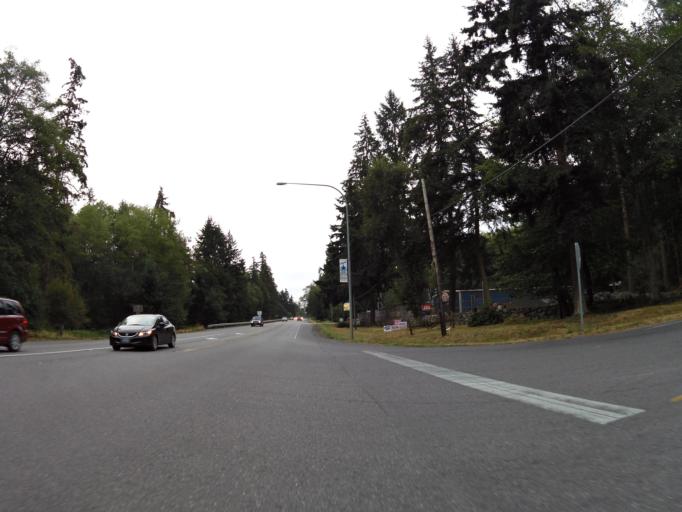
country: US
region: Washington
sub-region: Jefferson County
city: Port Townsend
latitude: 48.0971
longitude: -122.8152
